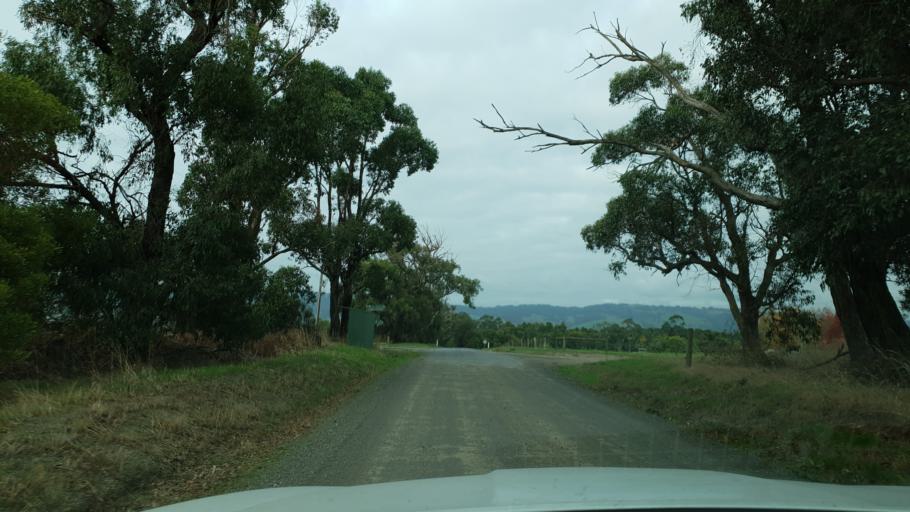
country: AU
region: Victoria
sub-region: Latrobe
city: Moe
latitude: -38.1731
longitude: 146.1310
